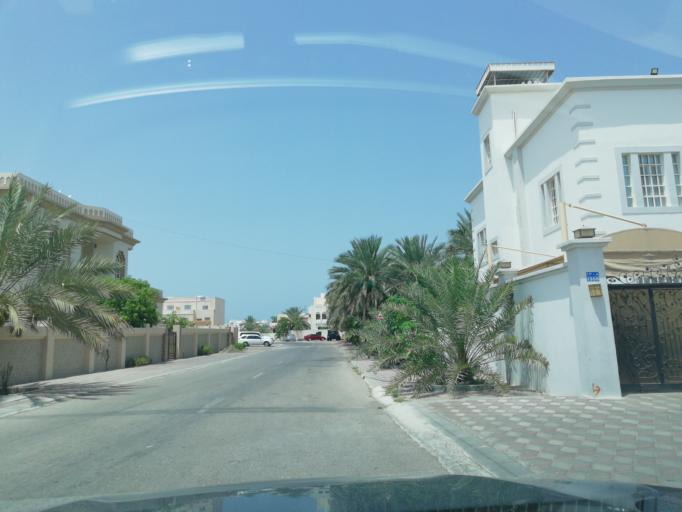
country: OM
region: Muhafazat Masqat
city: As Sib al Jadidah
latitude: 23.6586
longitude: 58.1936
